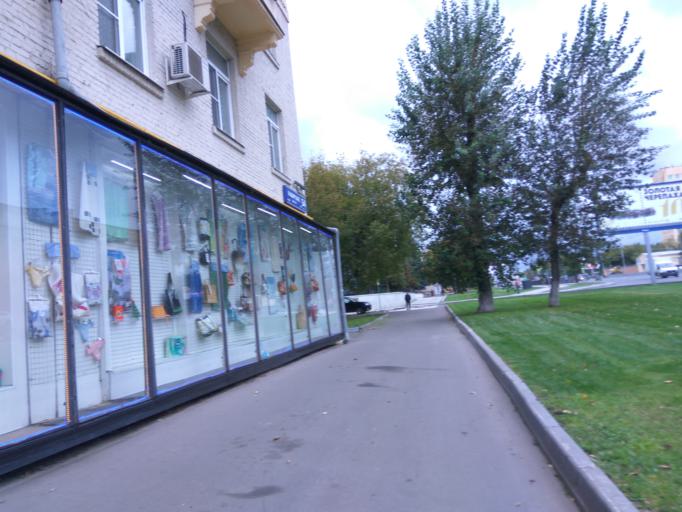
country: RU
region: Moscow
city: Kolomenskoye
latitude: 55.6461
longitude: 37.6700
